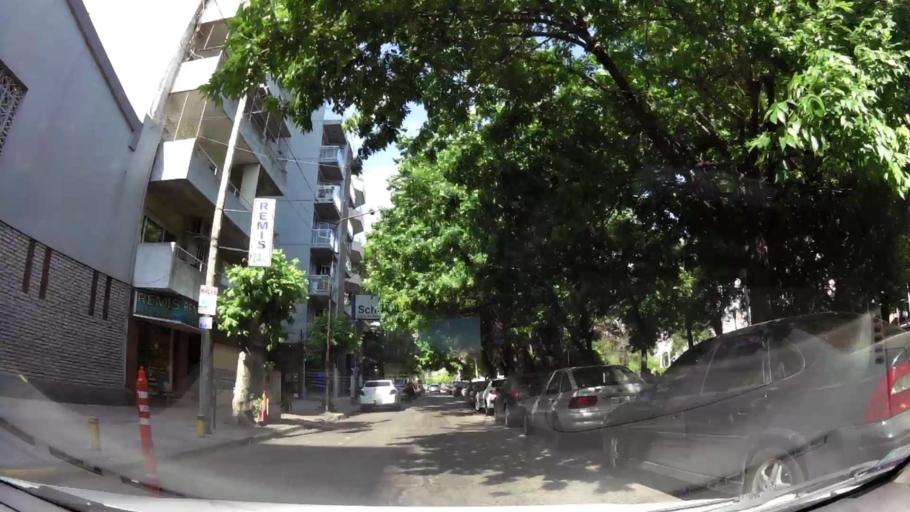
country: AR
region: Buenos Aires
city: San Justo
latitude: -34.6413
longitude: -58.5609
